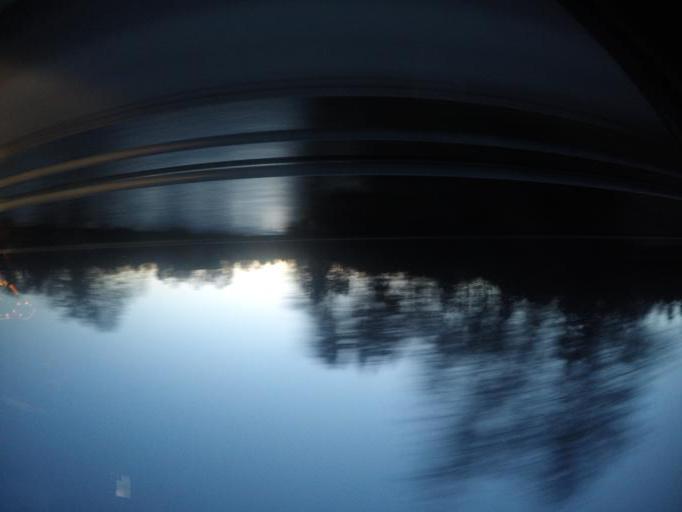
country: SE
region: Vaestmanland
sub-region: Arboga Kommun
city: Arboga
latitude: 59.4073
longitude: 15.7359
